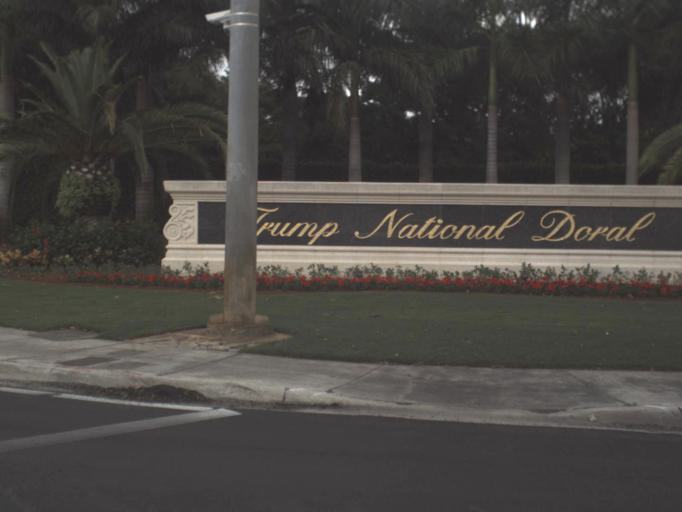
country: US
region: Florida
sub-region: Miami-Dade County
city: Doral
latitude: 25.8101
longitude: -80.3375
